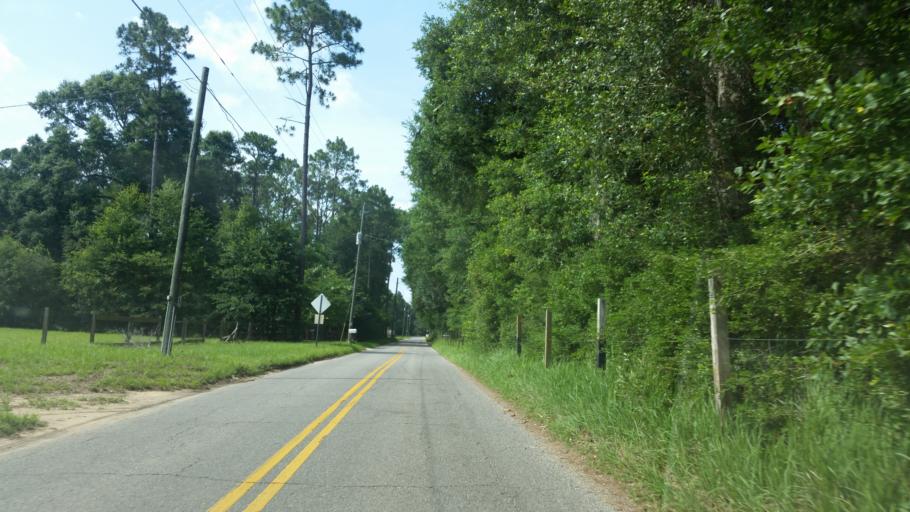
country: US
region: Florida
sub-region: Escambia County
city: Cantonment
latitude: 30.5695
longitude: -87.3624
